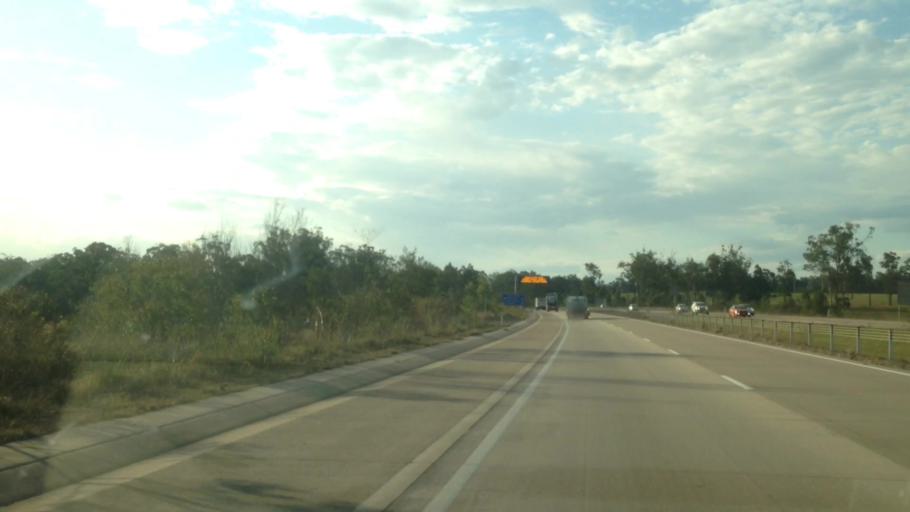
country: AU
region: New South Wales
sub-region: Cessnock
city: Heddon Greta
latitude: -32.8377
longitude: 151.5399
